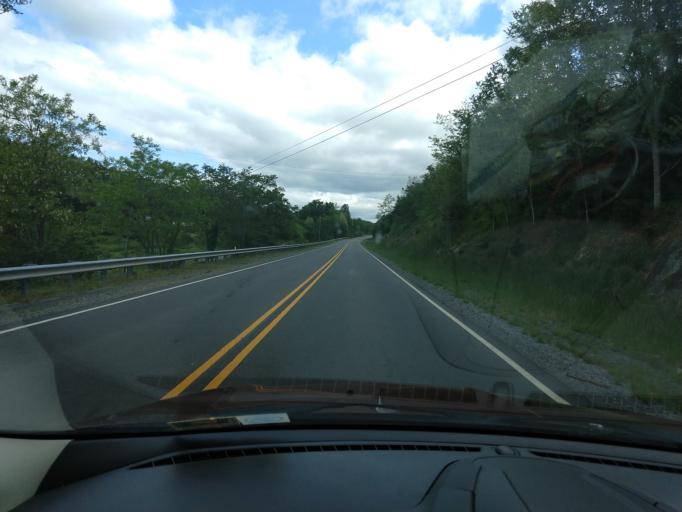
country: US
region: Virginia
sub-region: Wythe County
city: Wytheville
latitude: 36.8681
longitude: -80.9837
